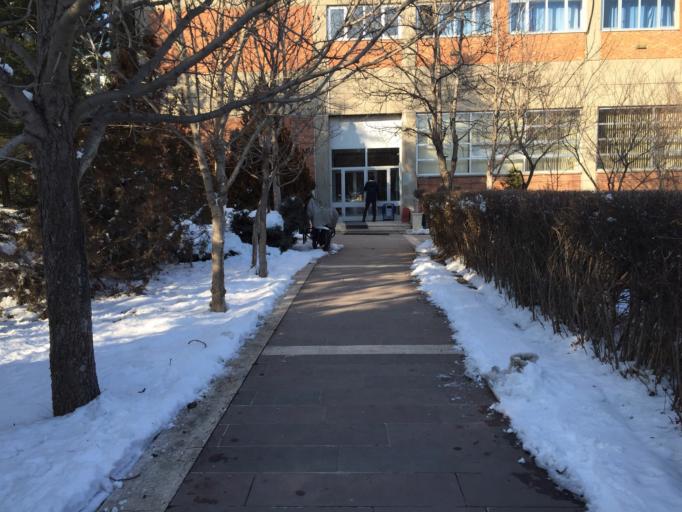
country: TR
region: Ankara
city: Ankara
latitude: 39.8898
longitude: 32.7837
